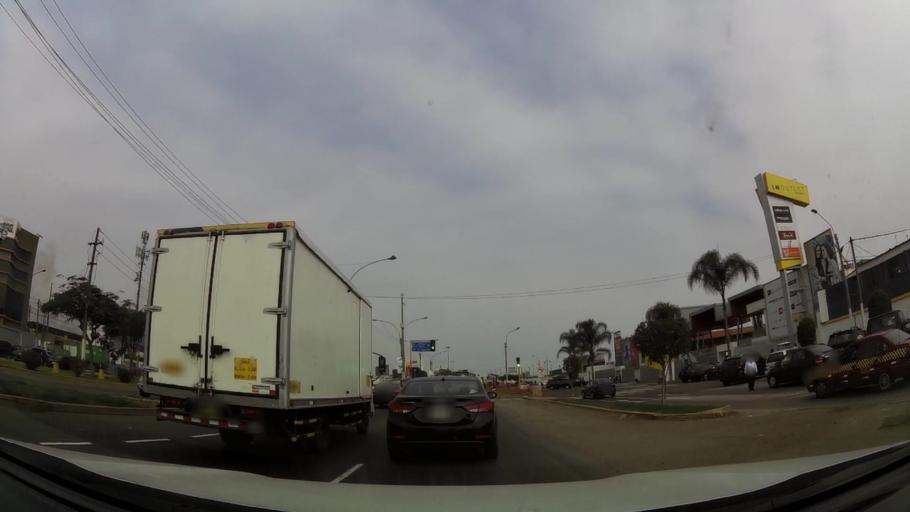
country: PE
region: Callao
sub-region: Callao
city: Callao
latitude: -12.0184
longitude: -77.1079
